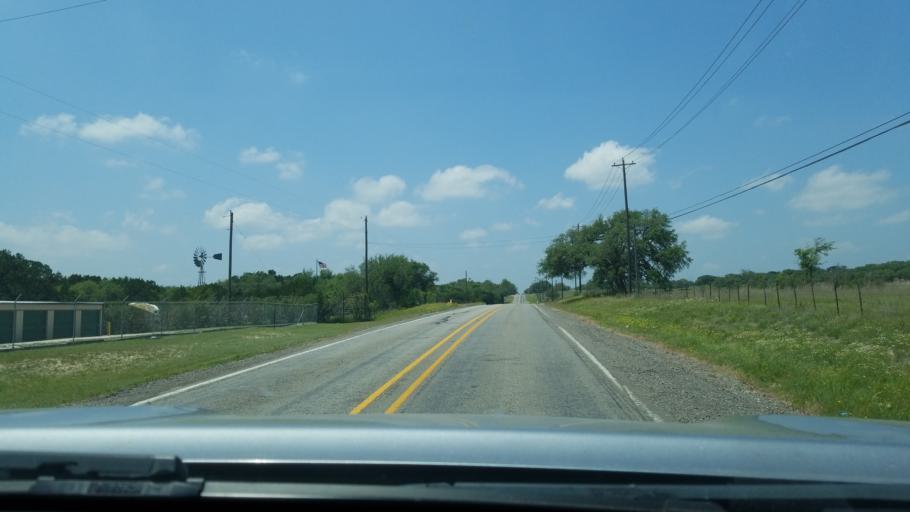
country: US
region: Texas
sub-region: Hays County
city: Woodcreek
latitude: 30.0369
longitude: -98.1835
